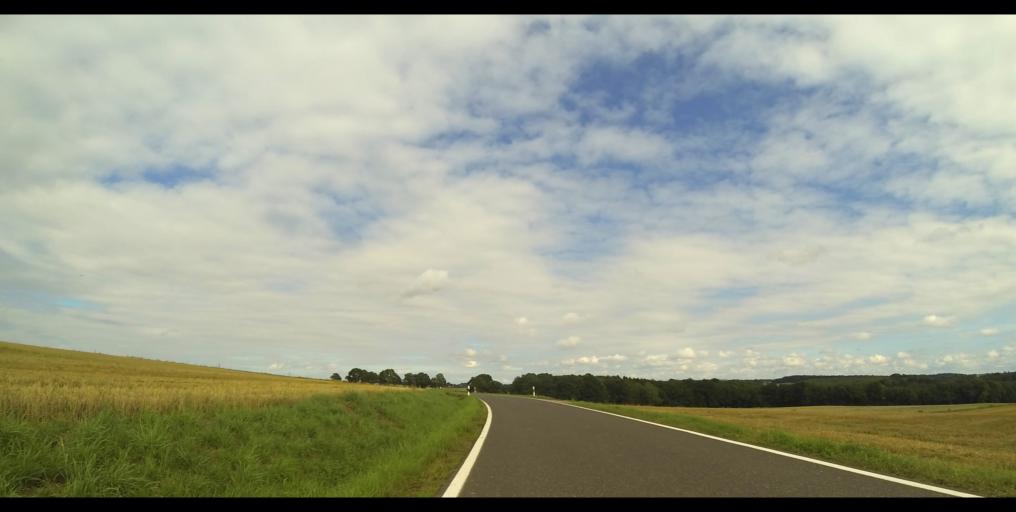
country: DE
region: Saxony
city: Grossschirma
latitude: 50.9873
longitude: 13.2170
